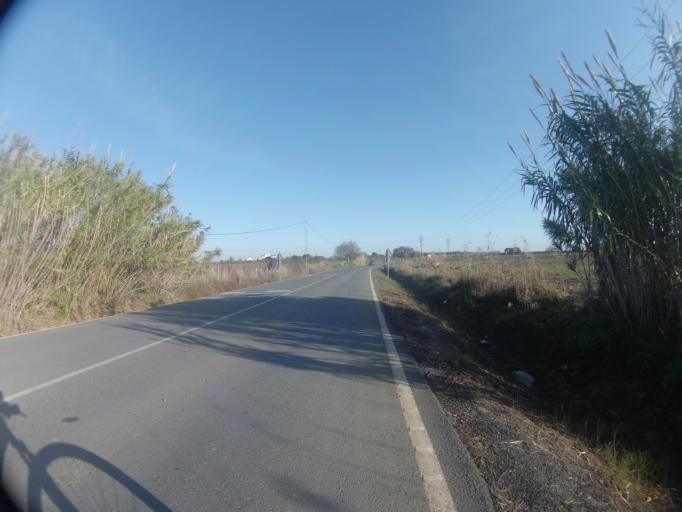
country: ES
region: Andalusia
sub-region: Provincia de Huelva
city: Huelva
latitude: 37.3168
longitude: -6.9136
